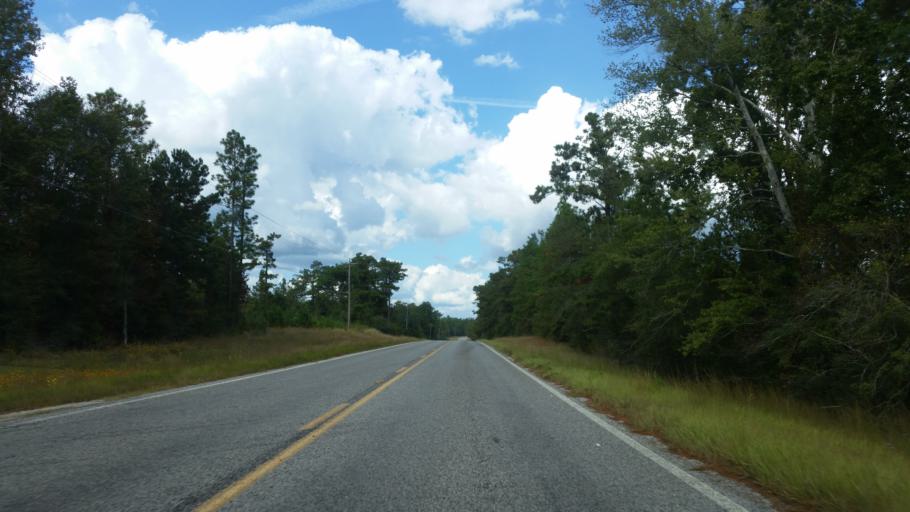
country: US
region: Mississippi
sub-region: Stone County
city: Wiggins
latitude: 30.8920
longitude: -89.1168
